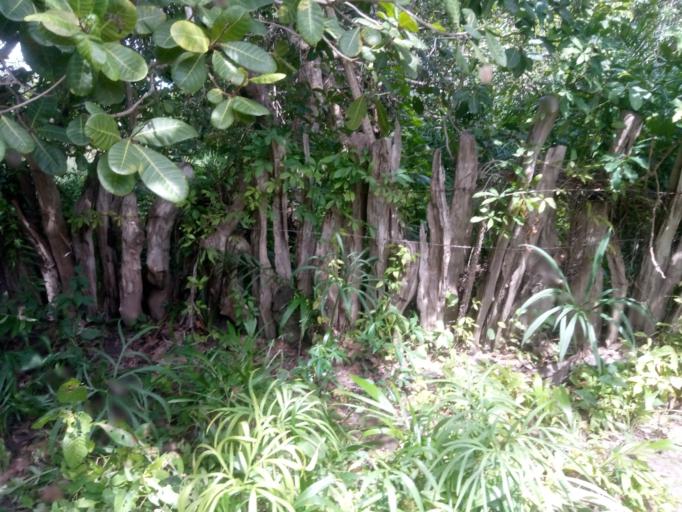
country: GM
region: Western
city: Gunjur
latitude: 13.0529
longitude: -16.7294
